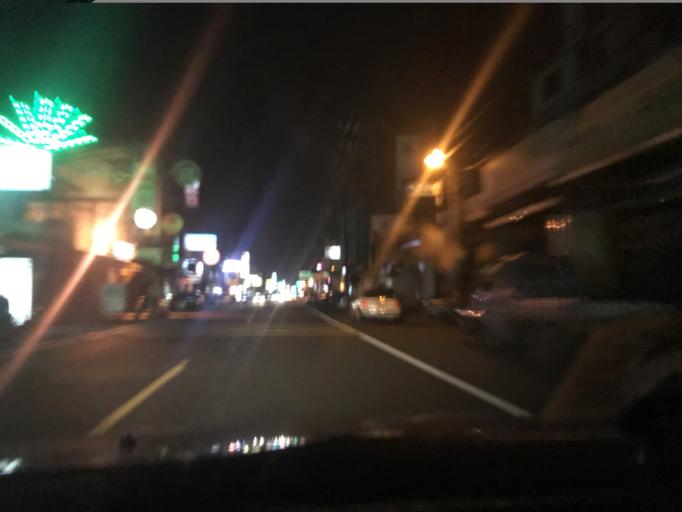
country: TW
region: Taiwan
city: Daxi
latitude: 24.9232
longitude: 121.2486
